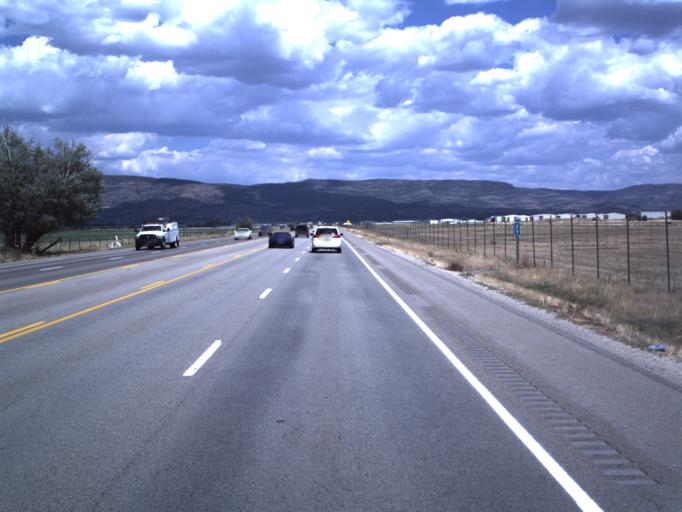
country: US
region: Utah
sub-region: Wasatch County
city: Heber
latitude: 40.4750
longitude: -111.4411
